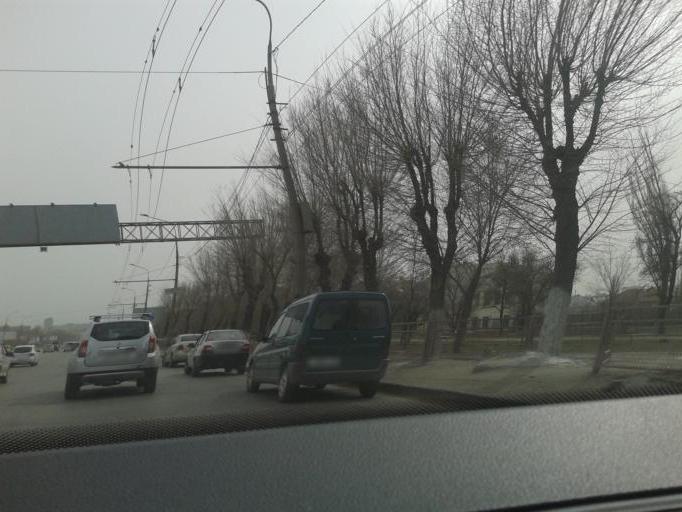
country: RU
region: Volgograd
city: Volgograd
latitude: 48.7501
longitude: 44.4849
